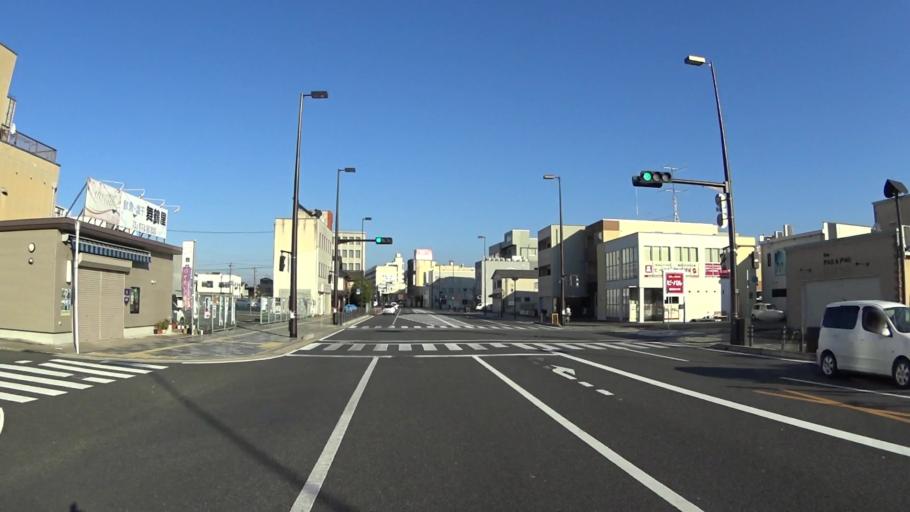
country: JP
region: Kyoto
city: Fukuchiyama
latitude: 35.2991
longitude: 135.1200
